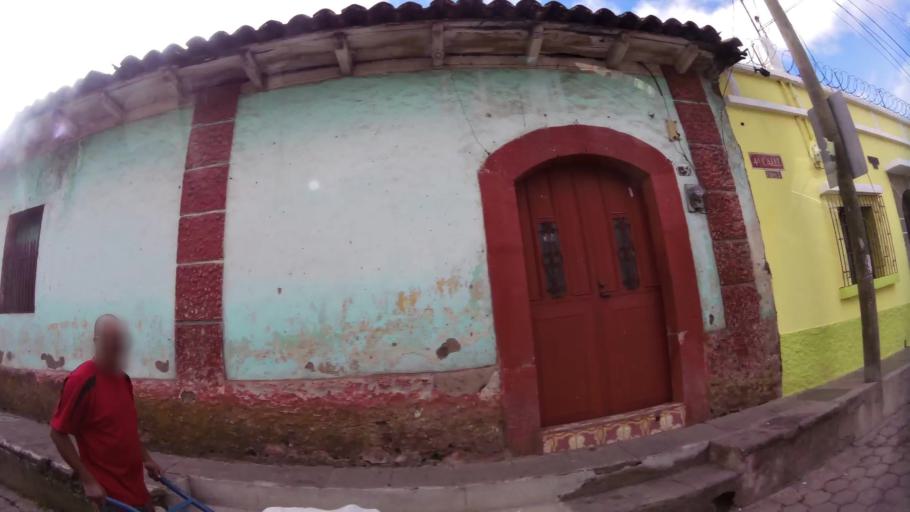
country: GT
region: Quetzaltenango
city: Salcaja
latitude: 14.8768
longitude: -91.4560
